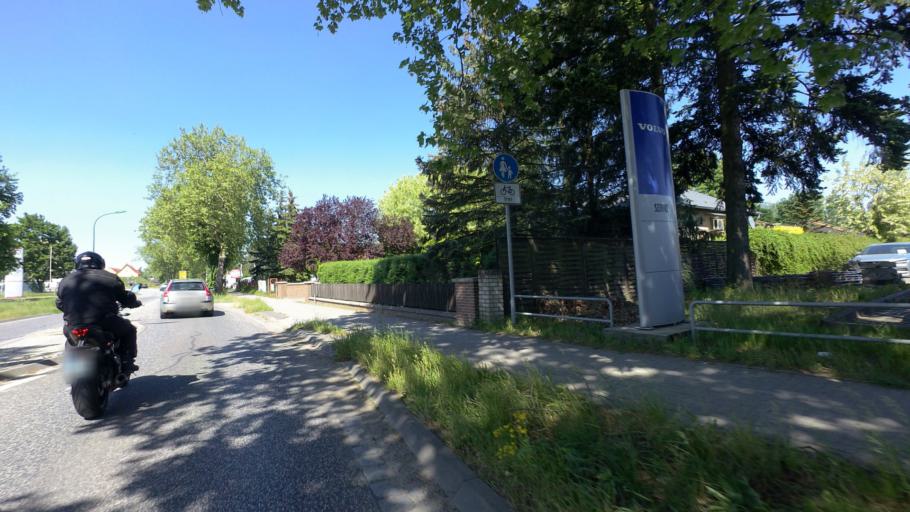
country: DE
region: Brandenburg
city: Konigs Wusterhausen
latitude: 52.2738
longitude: 13.6324
